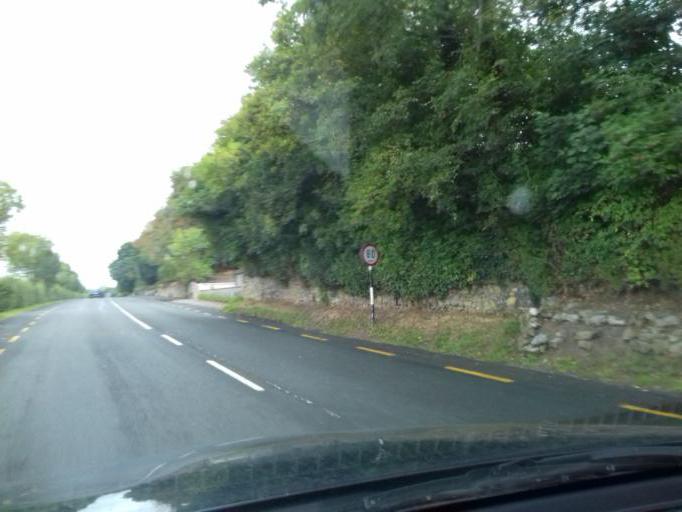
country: IE
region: Leinster
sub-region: County Carlow
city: Bagenalstown
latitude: 52.7383
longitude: -6.9752
